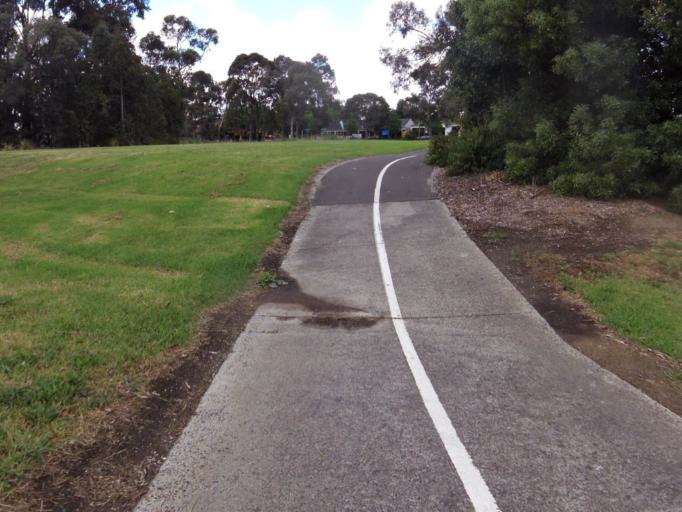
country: AU
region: Victoria
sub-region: Knox
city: Scoresby
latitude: -37.9117
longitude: 145.2366
